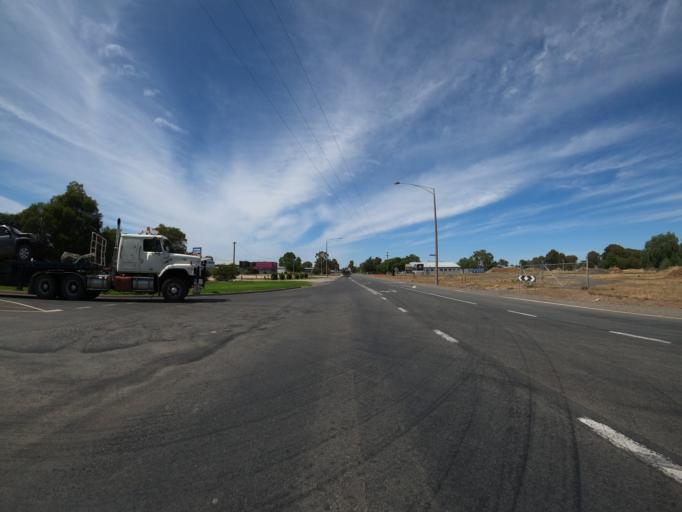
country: AU
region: Victoria
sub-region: Moira
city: Yarrawonga
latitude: -36.0269
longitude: 145.9956
